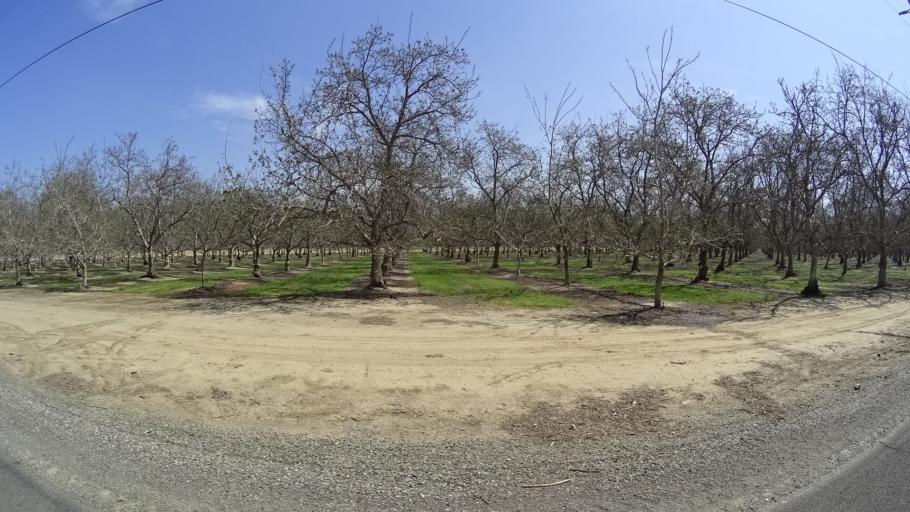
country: US
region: California
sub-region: Glenn County
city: Willows
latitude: 39.4748
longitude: -122.0189
